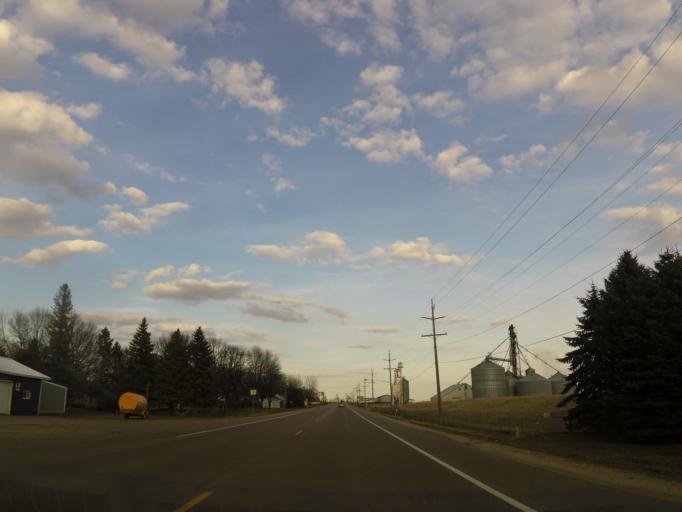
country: US
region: Minnesota
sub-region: McLeod County
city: Hutchinson
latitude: 44.7204
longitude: -94.4876
